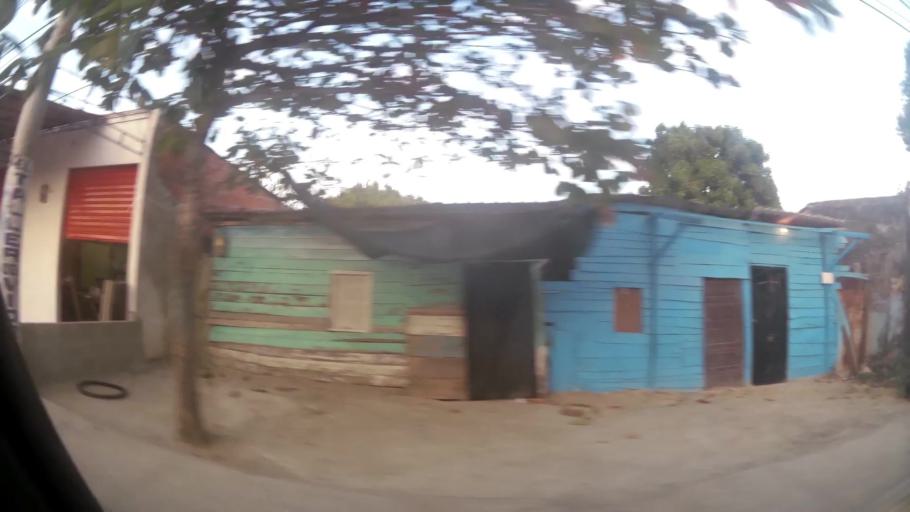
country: CO
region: Atlantico
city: Barranquilla
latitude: 10.9600
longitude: -74.8263
